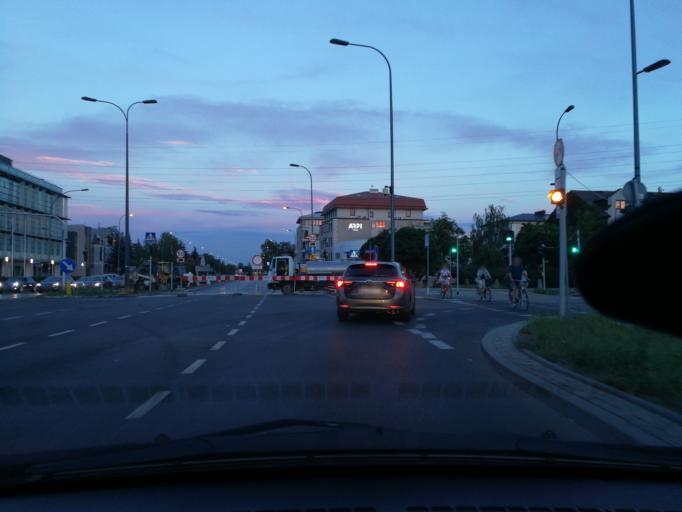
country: PL
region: Masovian Voivodeship
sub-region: Warszawa
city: Wilanow
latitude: 52.1793
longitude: 21.0717
